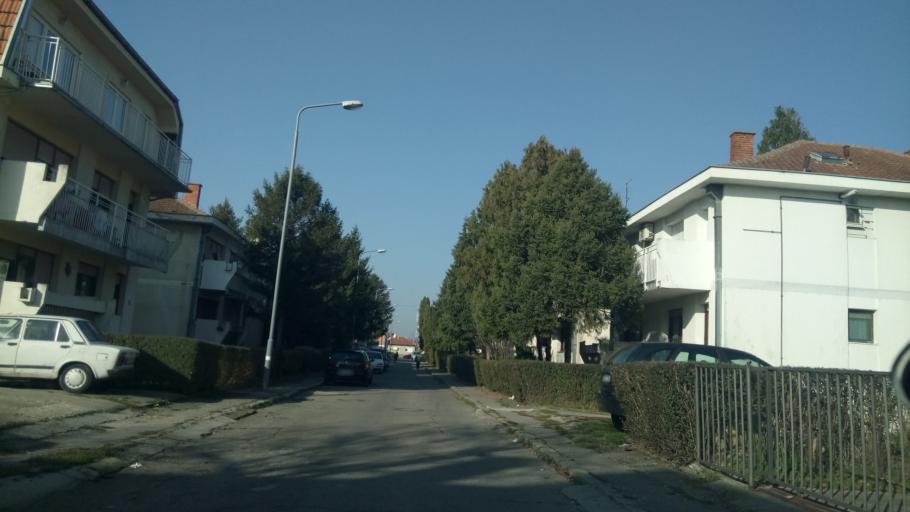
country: RS
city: Novi Banovci
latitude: 44.9025
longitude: 20.2852
